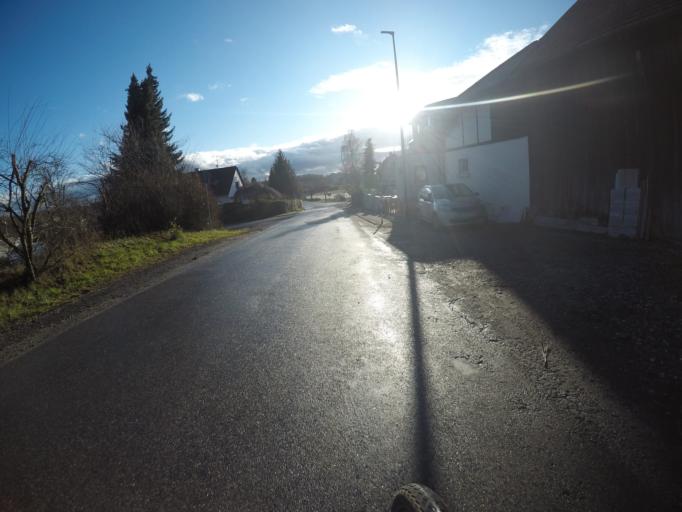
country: DE
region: Baden-Wuerttemberg
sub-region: Regierungsbezirk Stuttgart
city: Bondorf
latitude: 48.5299
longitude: 8.8737
